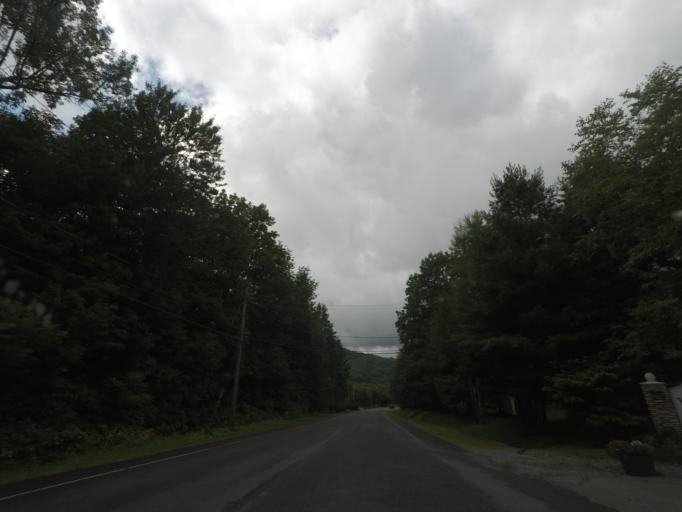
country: US
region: Massachusetts
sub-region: Berkshire County
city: Lanesborough
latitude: 42.5613
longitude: -73.2879
